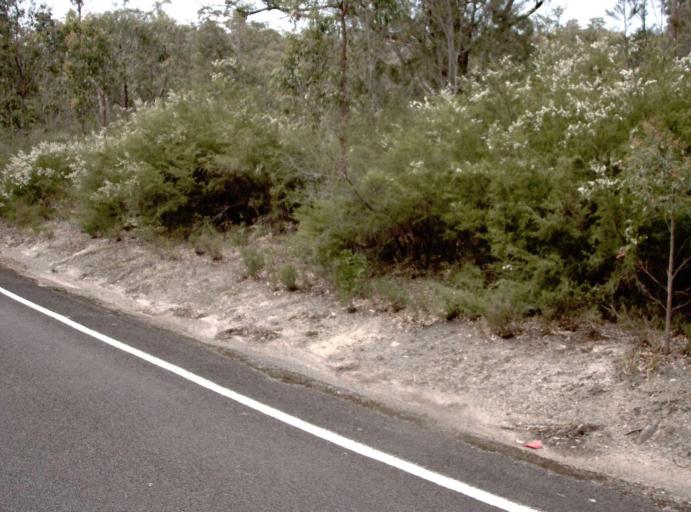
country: AU
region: New South Wales
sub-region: Bega Valley
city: Eden
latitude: -37.4877
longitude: 149.5502
